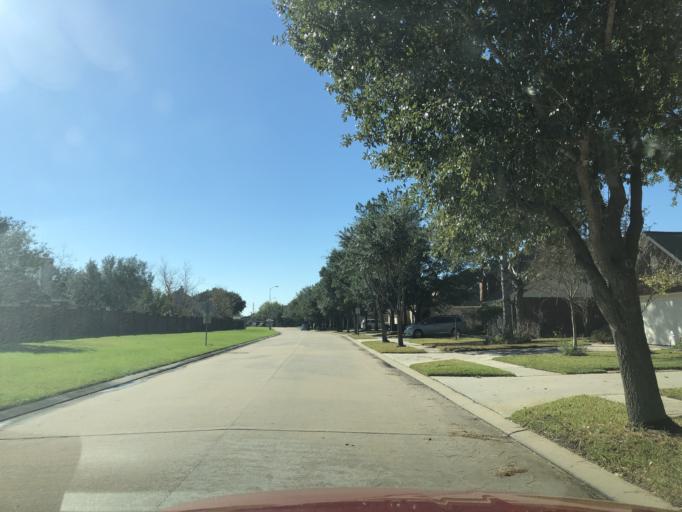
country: US
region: Texas
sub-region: Harris County
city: Oak Cliff Place
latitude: 29.9398
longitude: -95.6644
